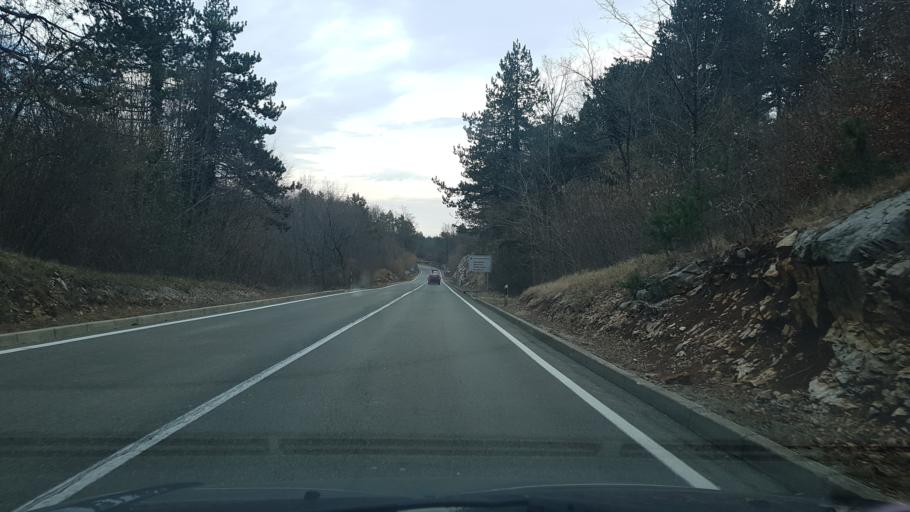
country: SI
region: Ilirska Bistrica
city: Ilirska Bistrica
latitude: 45.4912
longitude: 14.2219
